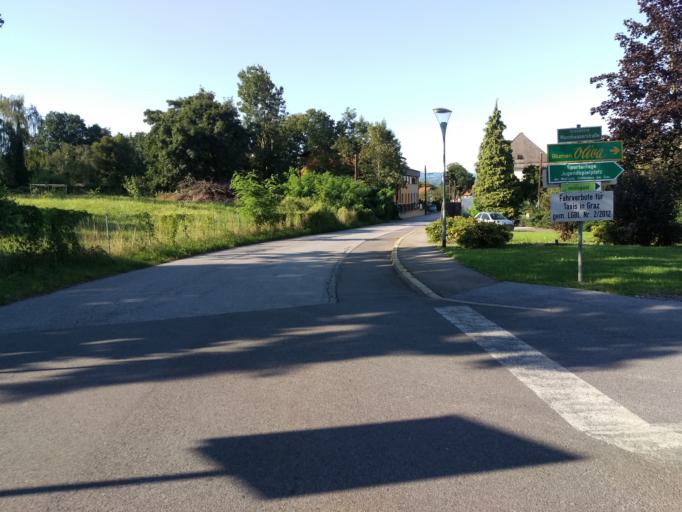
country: AT
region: Styria
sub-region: Politischer Bezirk Graz-Umgebung
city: Feldkirchen bei Graz
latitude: 47.0135
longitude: 15.4434
